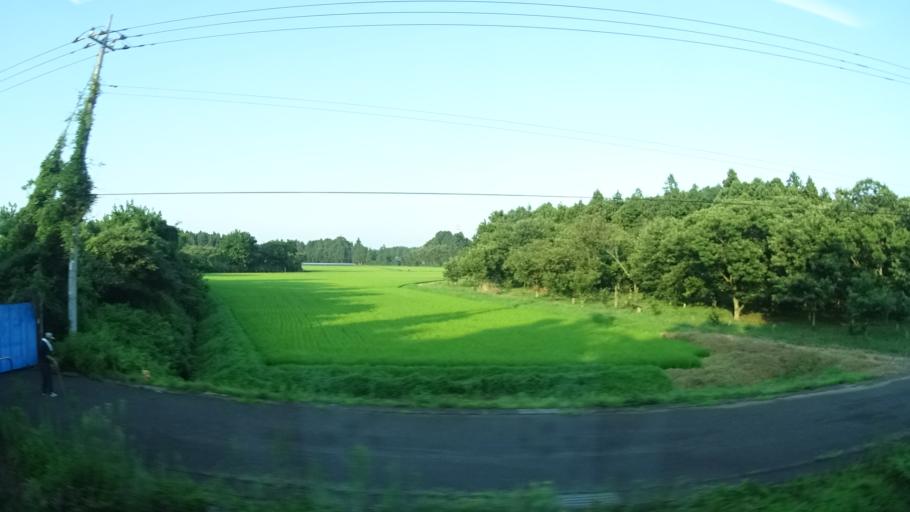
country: JP
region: Ibaraki
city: Ishioka
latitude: 36.2629
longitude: 140.2831
